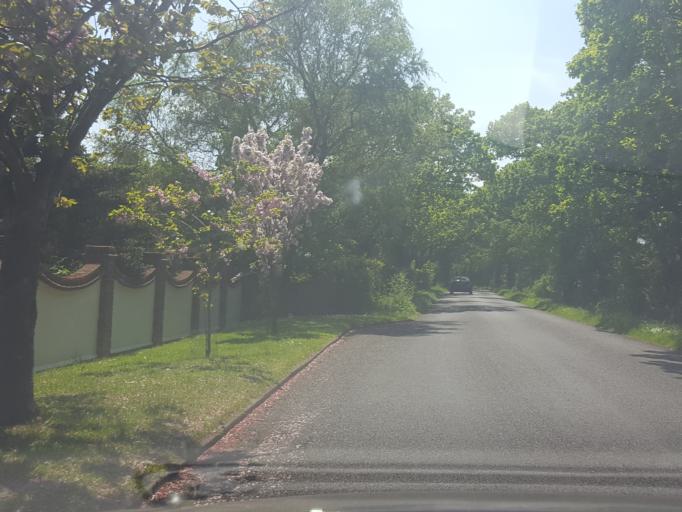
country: GB
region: England
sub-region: Essex
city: Great Bentley
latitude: 51.8607
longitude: 1.0914
